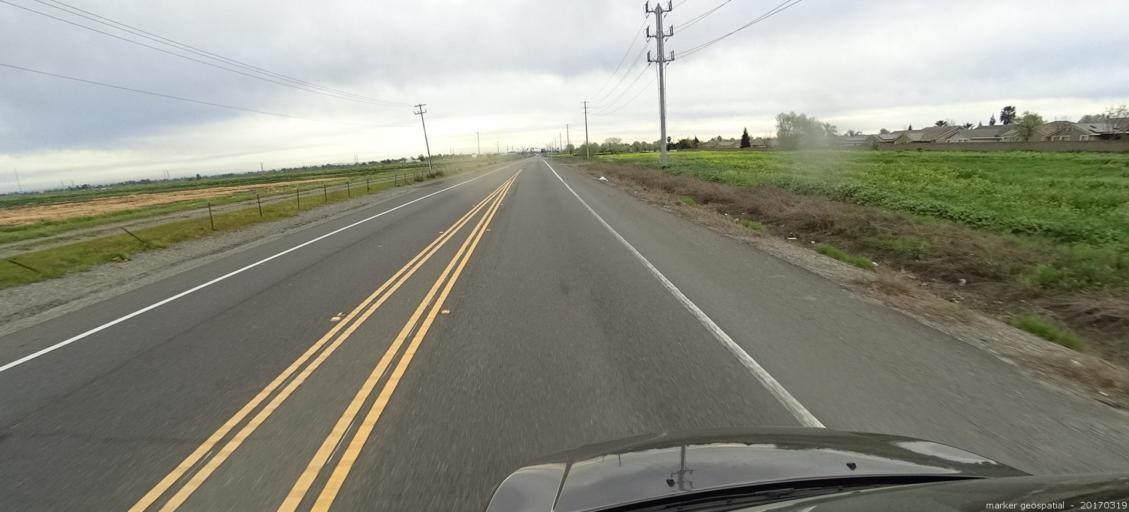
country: US
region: California
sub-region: Sacramento County
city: Elverta
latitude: 38.6852
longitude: -121.5051
